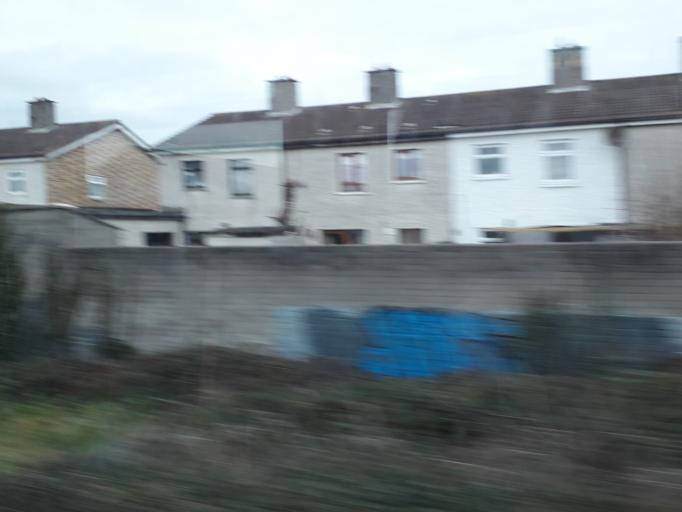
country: IE
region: Leinster
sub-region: Fingal County
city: Baldoyle
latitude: 53.3917
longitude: -6.1264
